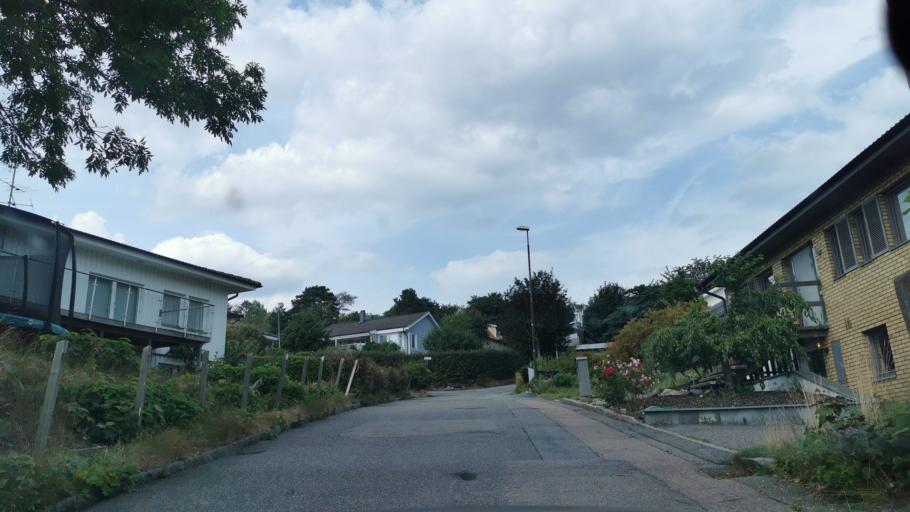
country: SE
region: Vaestra Goetaland
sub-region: Goteborg
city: Goeteborg
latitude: 57.6760
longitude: 11.9772
